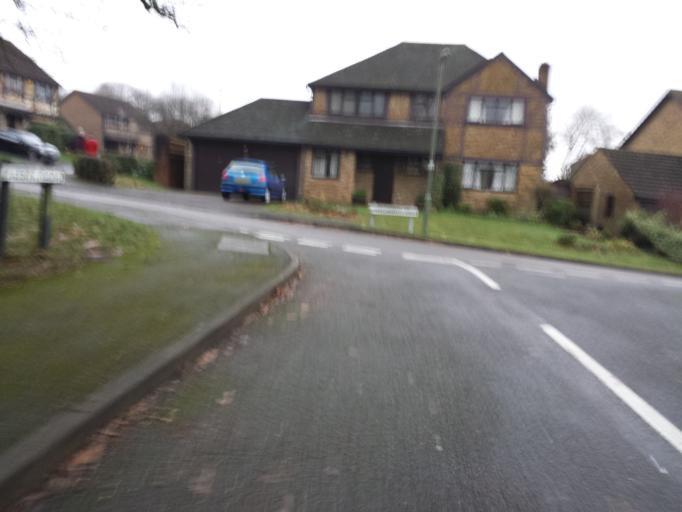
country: GB
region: England
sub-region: Surrey
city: Bagshot
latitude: 51.3529
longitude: -0.6940
